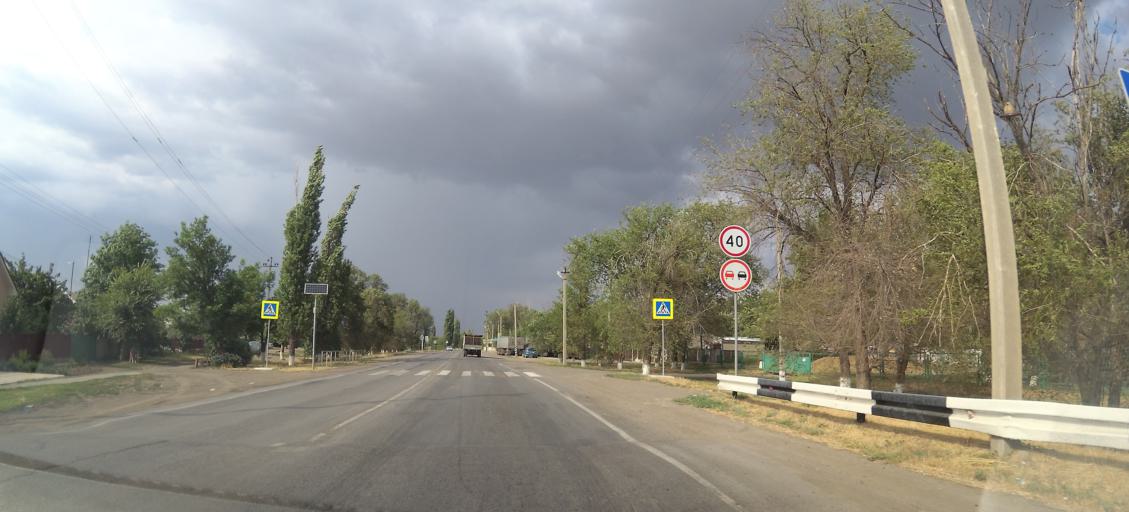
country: RU
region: Rostov
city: Zimovniki
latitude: 47.1469
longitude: 42.4586
